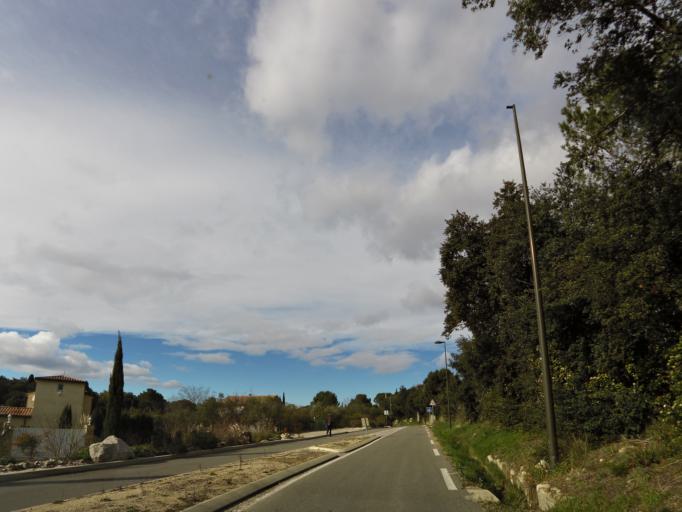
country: FR
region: Languedoc-Roussillon
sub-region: Departement du Gard
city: Aubais
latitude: 43.7505
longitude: 4.1619
